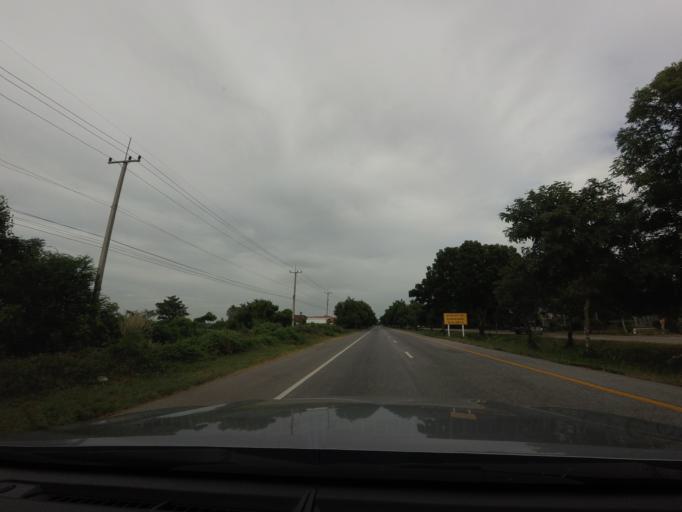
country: TH
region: Chai Nat
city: Sankhaburi
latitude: 15.0383
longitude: 100.1206
